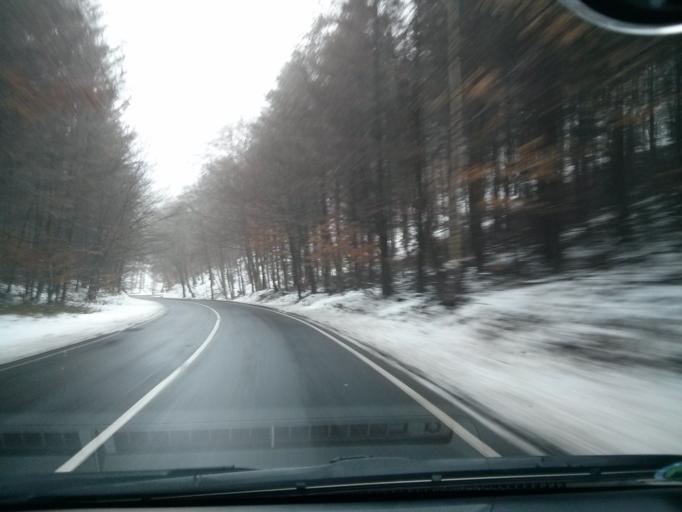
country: DE
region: Rheinland-Pfalz
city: Berg
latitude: 50.5789
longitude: 6.9381
